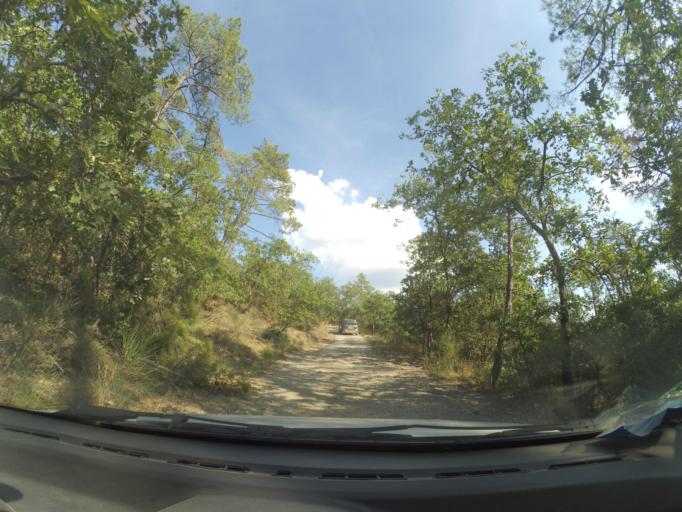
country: IT
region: Tuscany
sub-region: Province of Arezzo
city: Castiglion Fibocchi
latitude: 43.5323
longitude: 11.7845
